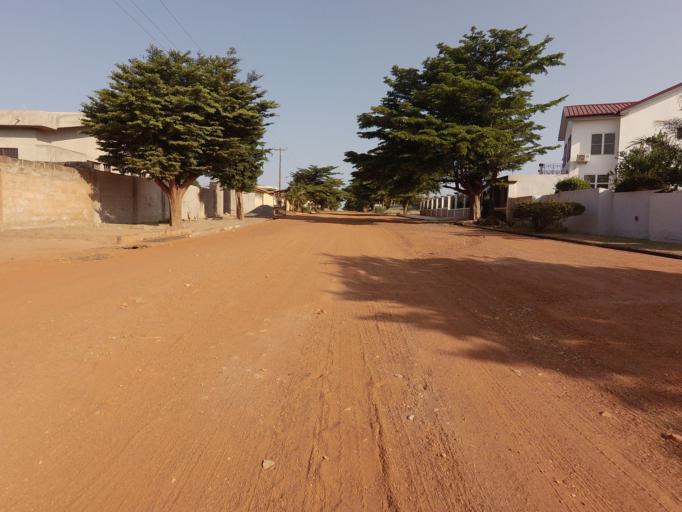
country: GH
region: Greater Accra
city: Nungua
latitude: 5.6398
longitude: -0.0865
